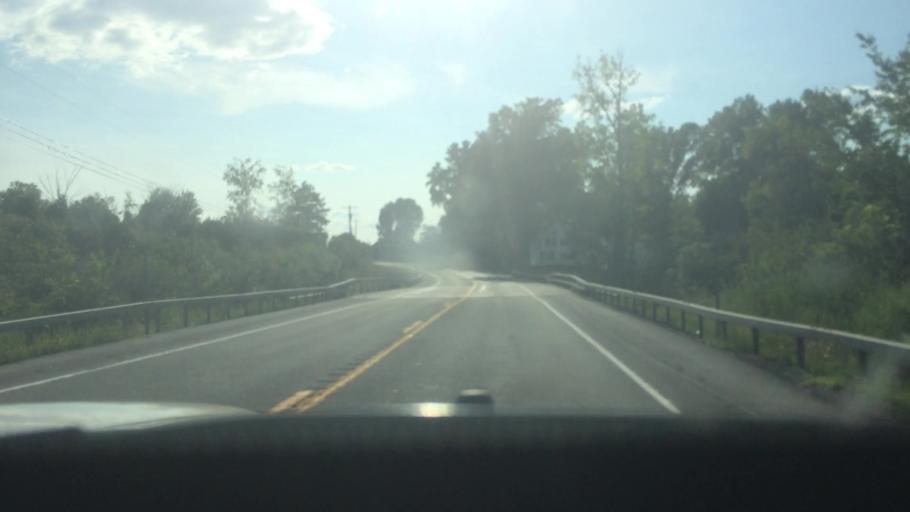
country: US
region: New York
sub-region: St. Lawrence County
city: Potsdam
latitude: 44.6852
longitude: -74.8034
